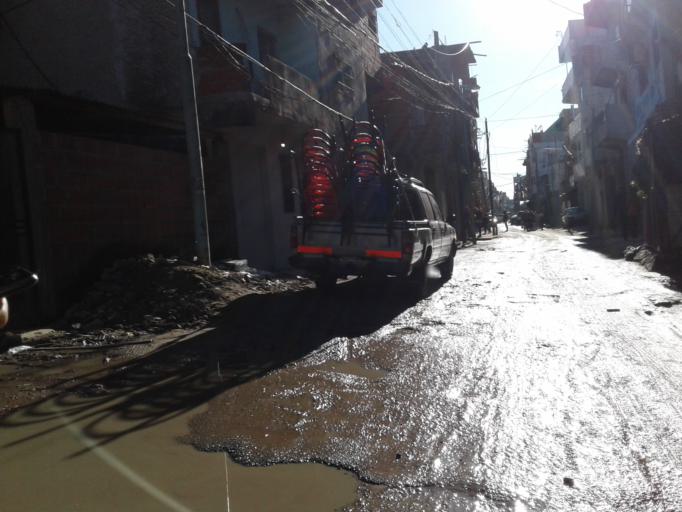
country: AR
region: Buenos Aires F.D.
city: Villa Lugano
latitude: -34.6758
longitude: -58.4650
